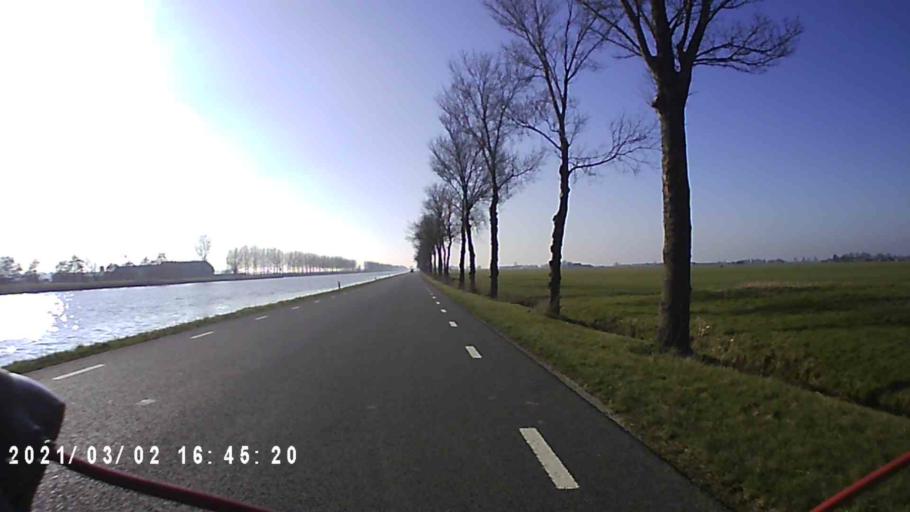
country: NL
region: Groningen
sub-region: Gemeente Zuidhorn
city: Grijpskerk
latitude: 53.2467
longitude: 6.2884
